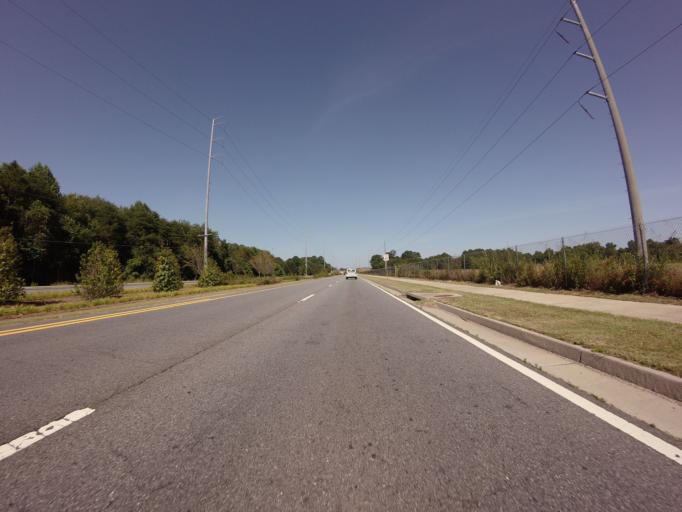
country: US
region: Georgia
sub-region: Gwinnett County
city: Suwanee
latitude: 34.0509
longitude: -84.1035
